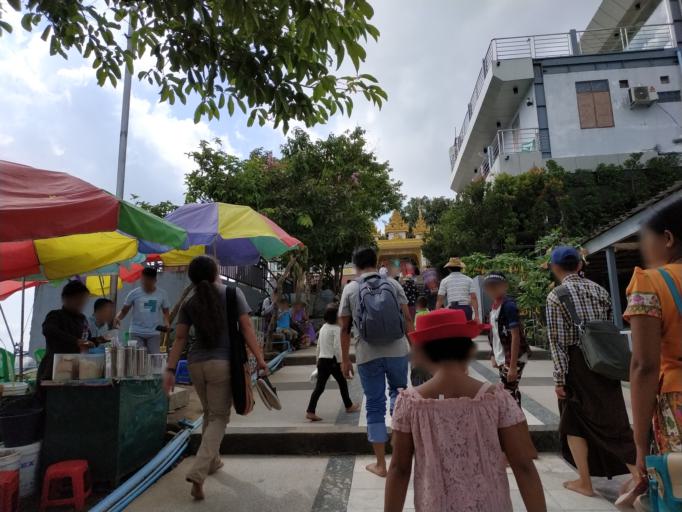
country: MM
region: Mon
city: Kyaikto
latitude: 17.4796
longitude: 97.1000
